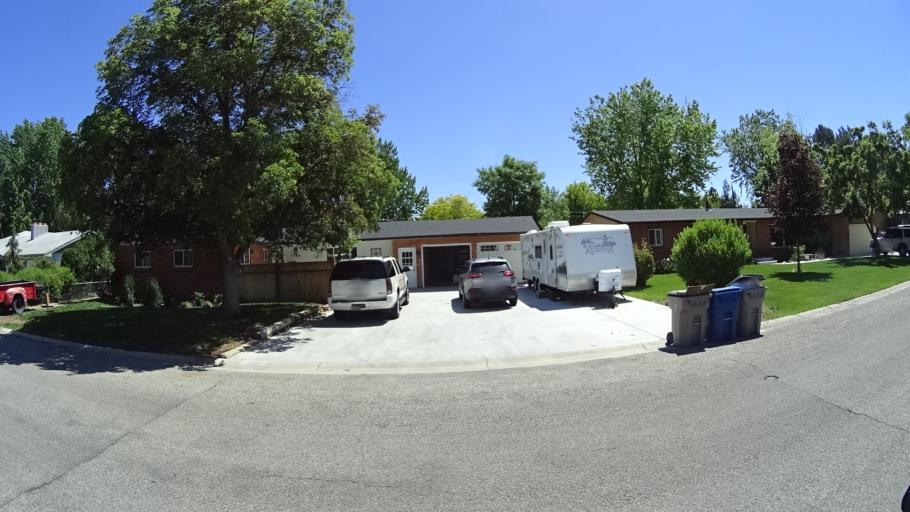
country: US
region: Idaho
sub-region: Ada County
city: Garden City
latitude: 43.5798
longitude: -116.2336
